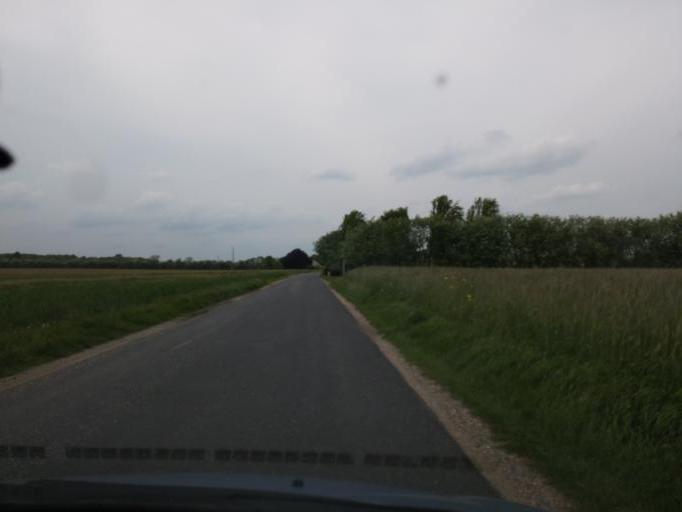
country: DK
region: South Denmark
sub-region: Odense Kommune
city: Bullerup
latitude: 55.4139
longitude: 10.4981
